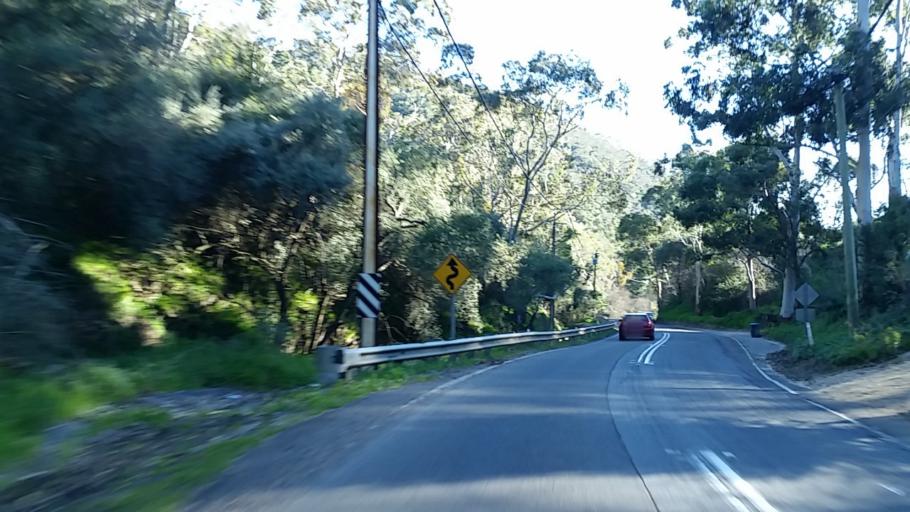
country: AU
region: South Australia
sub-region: Adelaide Hills
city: Adelaide Hills
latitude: -34.9213
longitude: 138.7086
